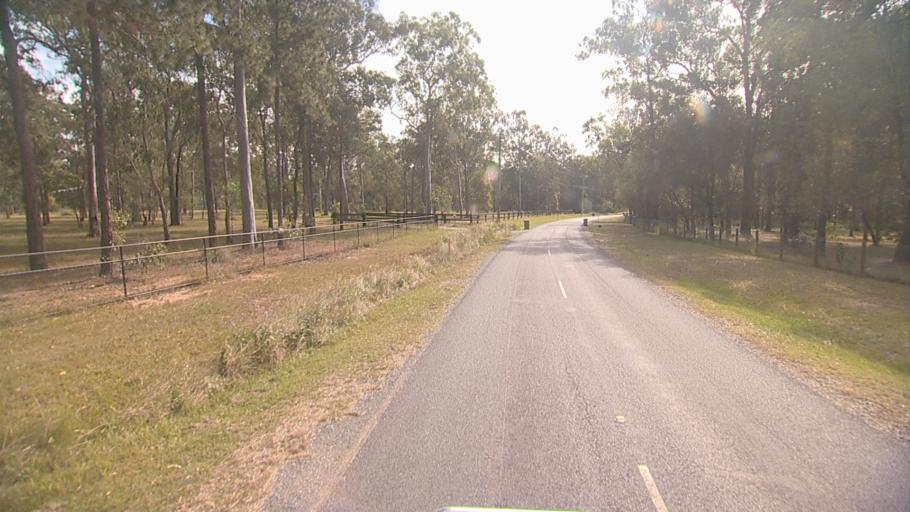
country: AU
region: Queensland
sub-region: Logan
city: North Maclean
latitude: -27.7527
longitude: 152.9737
